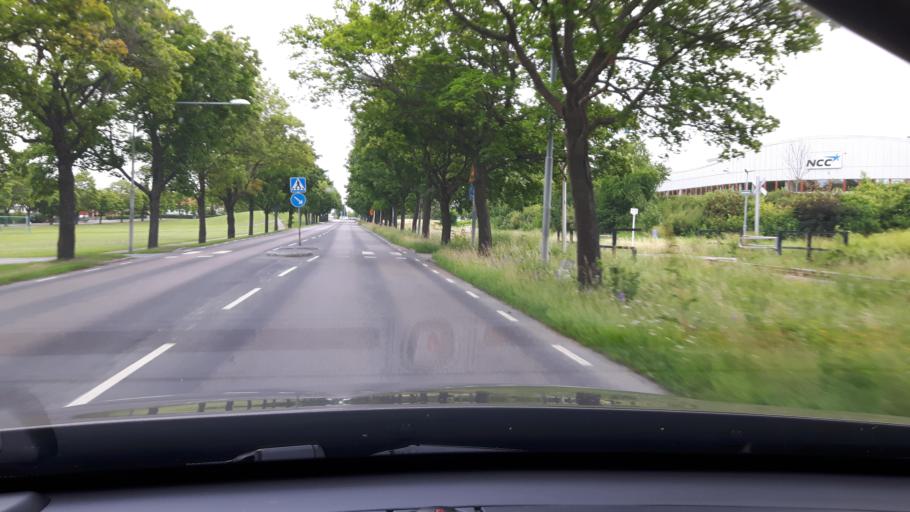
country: SE
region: Uppsala
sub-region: Uppsala Kommun
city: Uppsala
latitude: 59.8578
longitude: 17.6700
